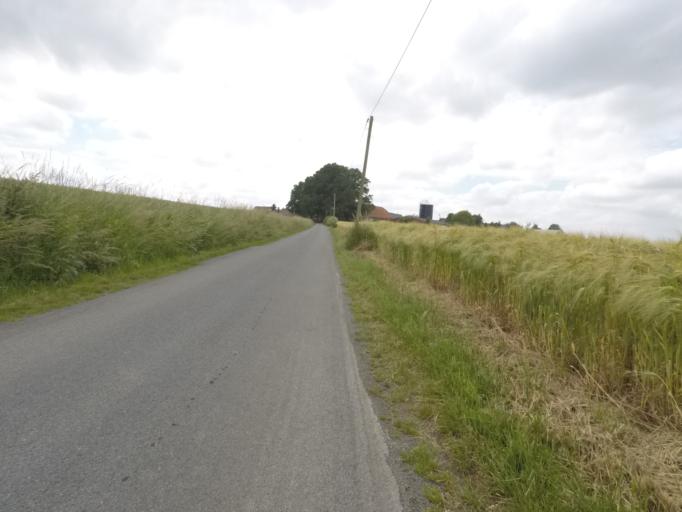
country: DE
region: North Rhine-Westphalia
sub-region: Regierungsbezirk Detmold
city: Werther
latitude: 52.0952
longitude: 8.4349
